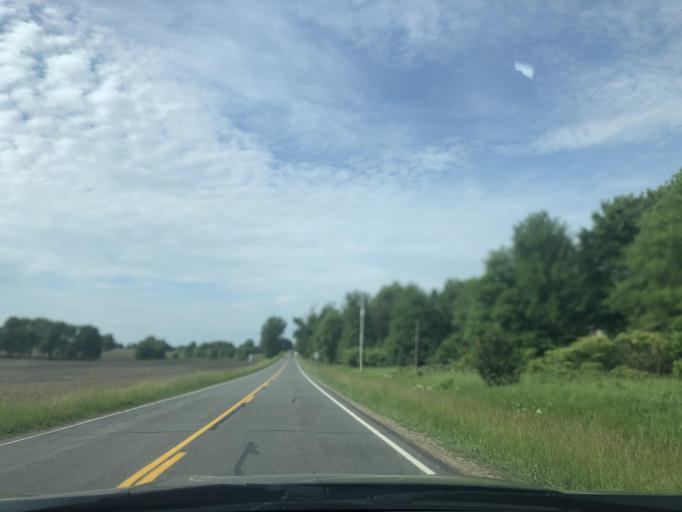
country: US
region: Michigan
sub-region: Clinton County
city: Bath
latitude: 42.8142
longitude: -84.4837
